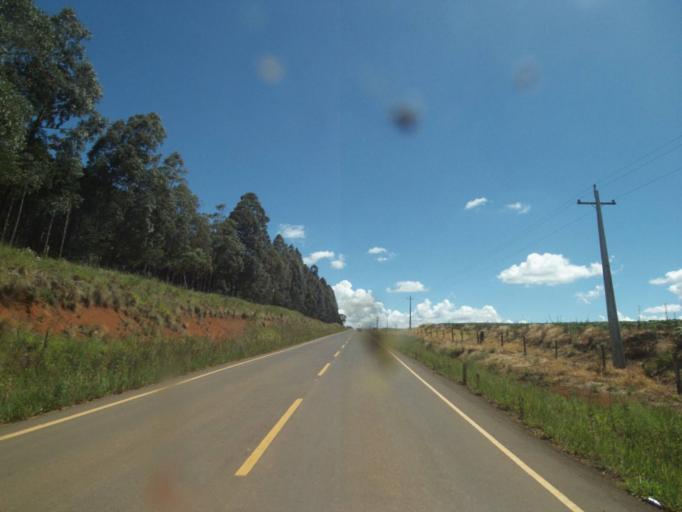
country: BR
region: Parana
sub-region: Pinhao
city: Pinhao
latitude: -25.8309
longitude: -52.0200
